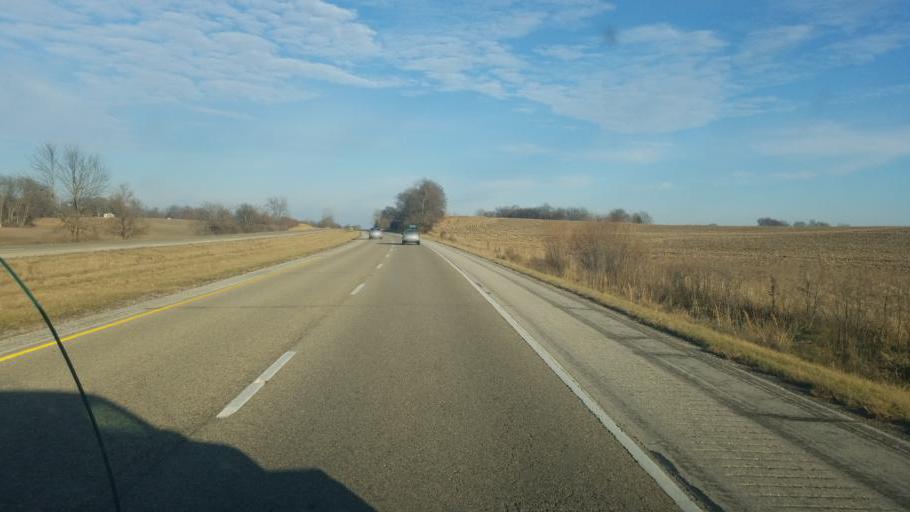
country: US
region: Indiana
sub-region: Knox County
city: Vincennes
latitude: 38.6759
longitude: -87.4256
